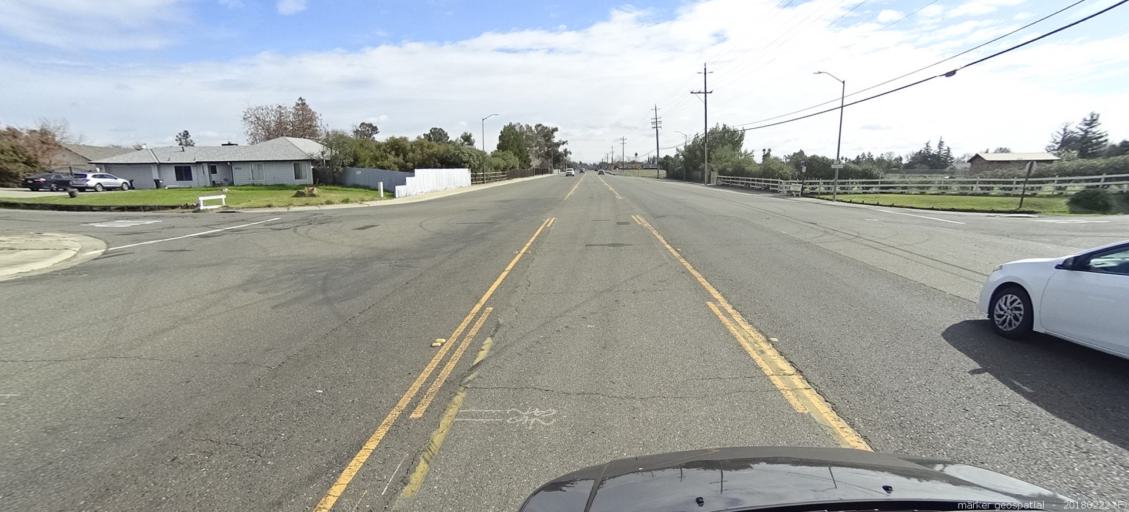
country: US
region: California
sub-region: Sacramento County
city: Rio Linda
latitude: 38.7144
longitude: -121.4193
